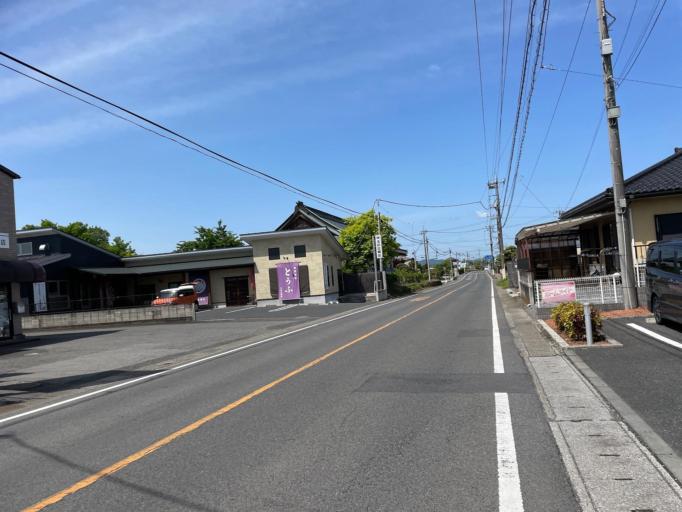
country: JP
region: Tochigi
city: Mibu
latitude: 36.4207
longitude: 139.7987
